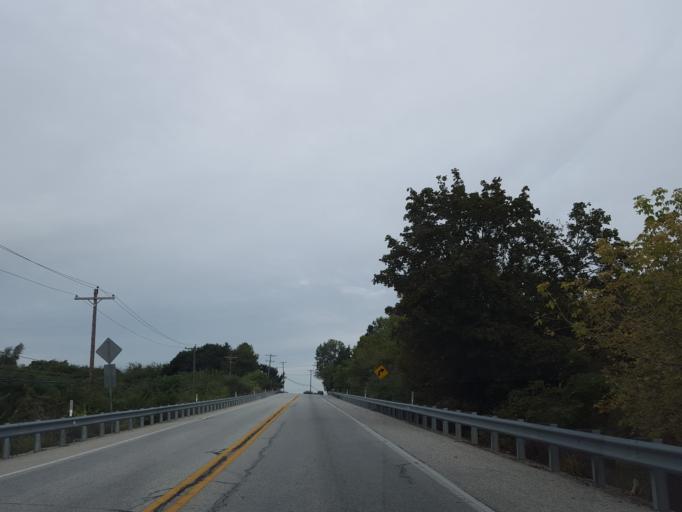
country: US
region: Pennsylvania
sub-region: York County
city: Shiloh
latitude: 39.9244
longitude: -76.8016
